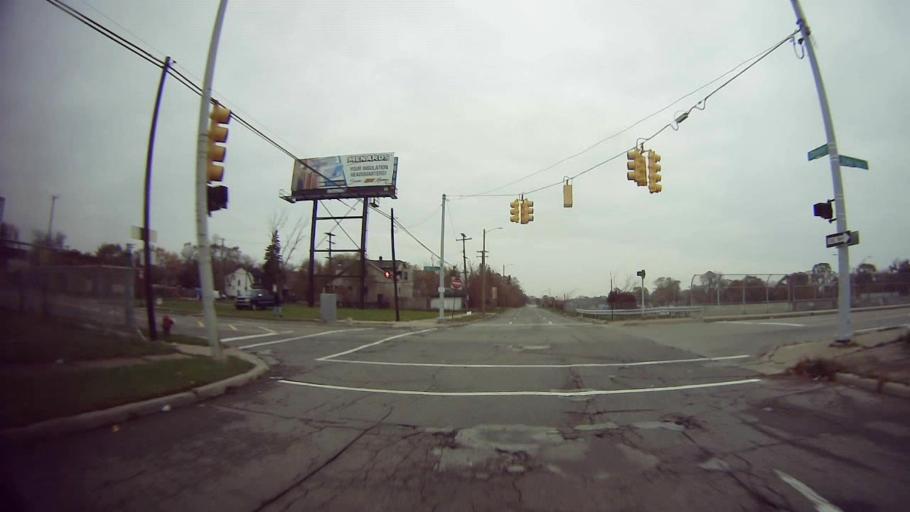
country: US
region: Michigan
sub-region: Oakland County
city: Hazel Park
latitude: 42.4395
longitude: -83.0956
